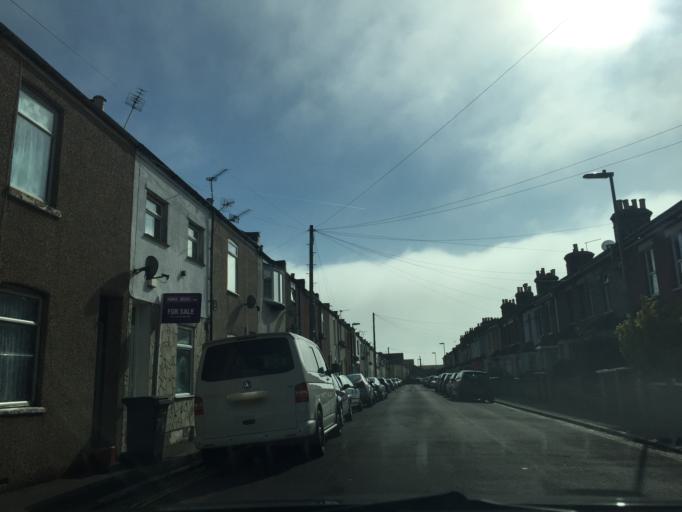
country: GB
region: England
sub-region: Hampshire
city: Gosport
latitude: 50.7906
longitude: -1.1319
